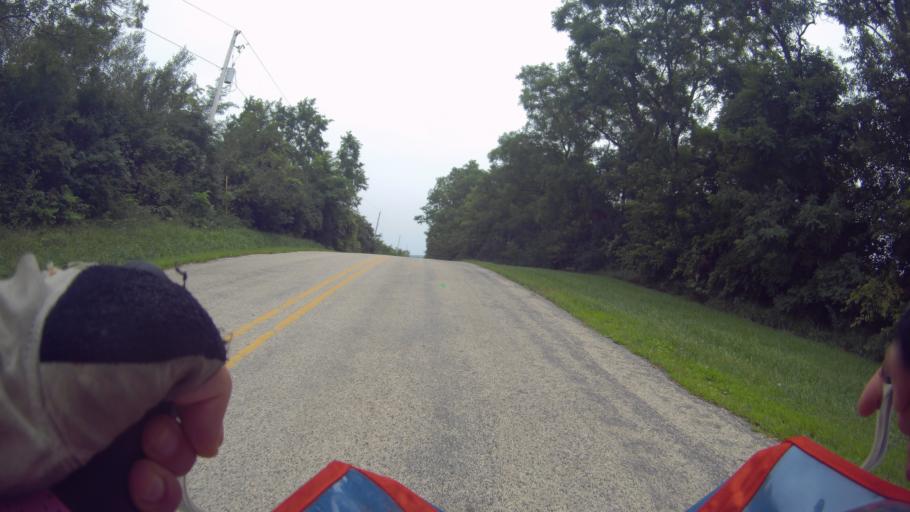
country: US
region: Wisconsin
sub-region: Dane County
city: Verona
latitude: 42.9734
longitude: -89.5730
